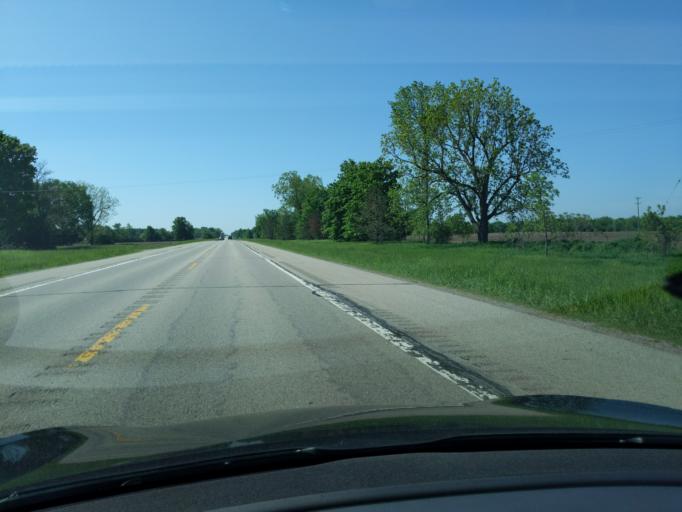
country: US
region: Michigan
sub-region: Ingham County
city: Webberville
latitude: 42.5908
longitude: -84.1934
